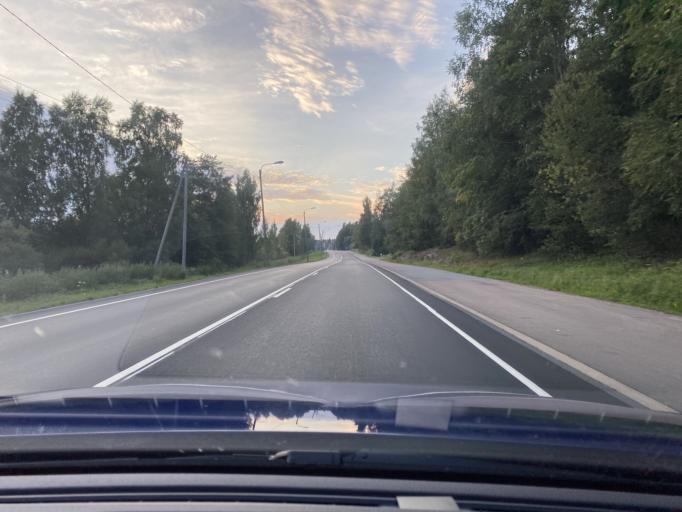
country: FI
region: Satakunta
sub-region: Pohjois-Satakunta
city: Kankaanpaeae
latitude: 61.8204
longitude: 22.3660
